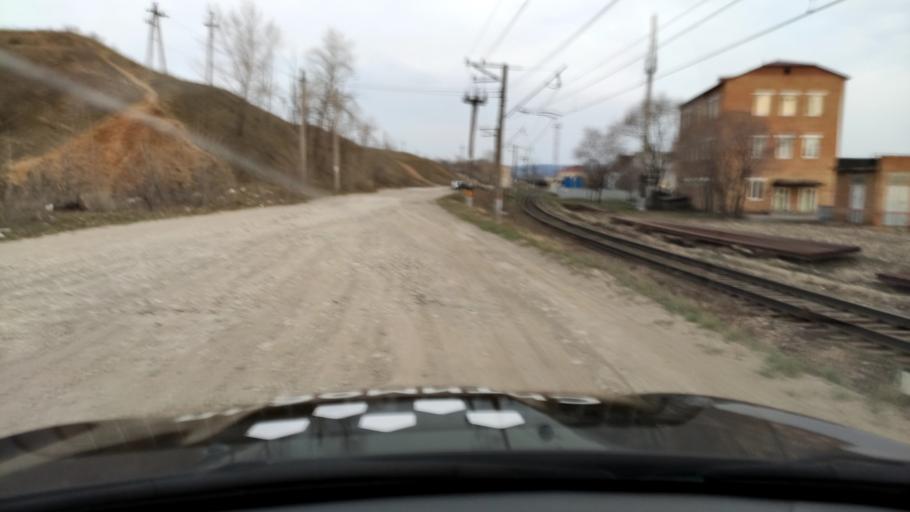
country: RU
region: Samara
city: Zhigulevsk
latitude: 53.4776
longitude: 49.5308
